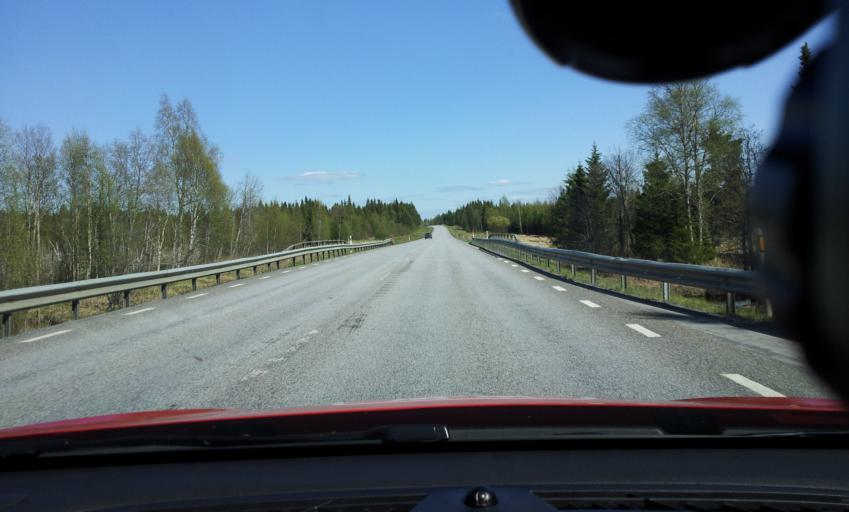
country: SE
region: Jaemtland
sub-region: Krokoms Kommun
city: Valla
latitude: 63.3122
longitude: 13.7435
